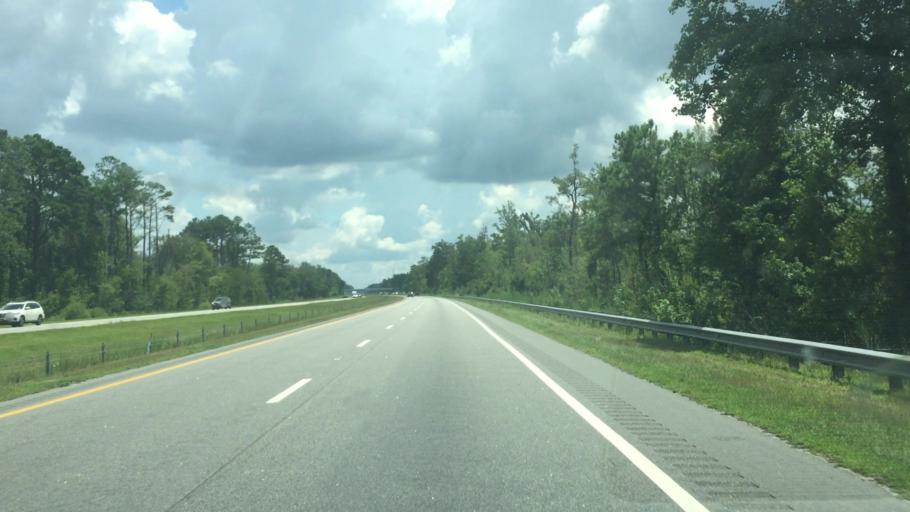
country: US
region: North Carolina
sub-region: Columbus County
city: Chadbourn
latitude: 34.4023
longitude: -78.9166
